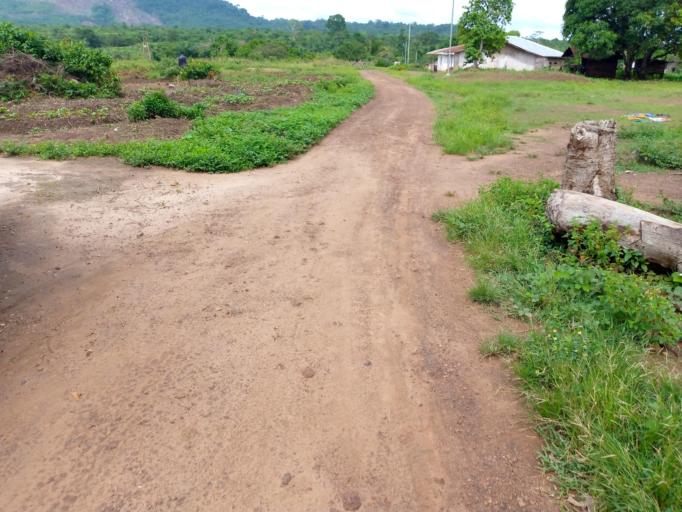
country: SL
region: Southern Province
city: Mogbwemo
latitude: 7.7618
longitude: -12.3125
